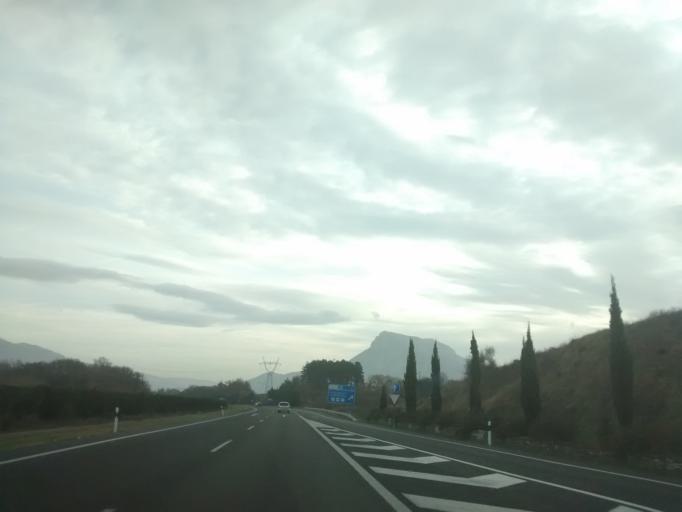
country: ES
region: Navarre
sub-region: Provincia de Navarra
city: Bakaiku
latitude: 42.8930
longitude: -2.0934
